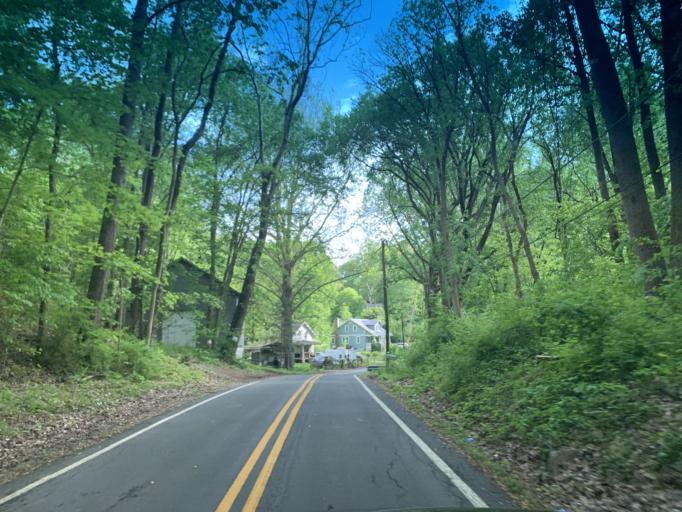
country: US
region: Maryland
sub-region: Cecil County
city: Rising Sun
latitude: 39.6900
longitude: -76.1861
